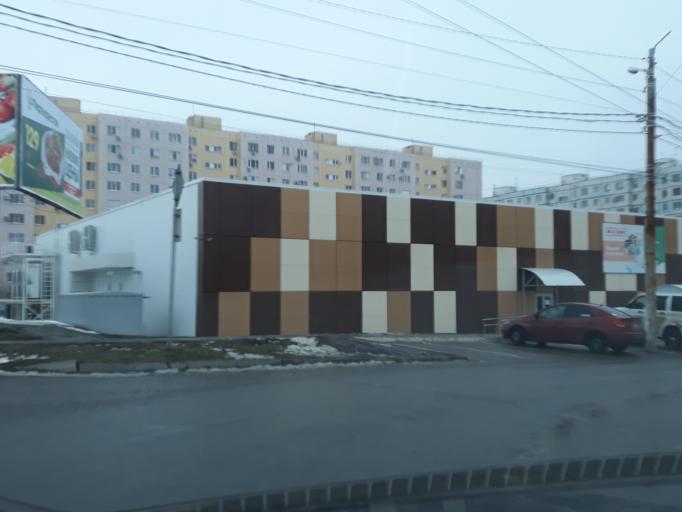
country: RU
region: Rostov
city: Taganrog
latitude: 47.2793
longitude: 38.9238
